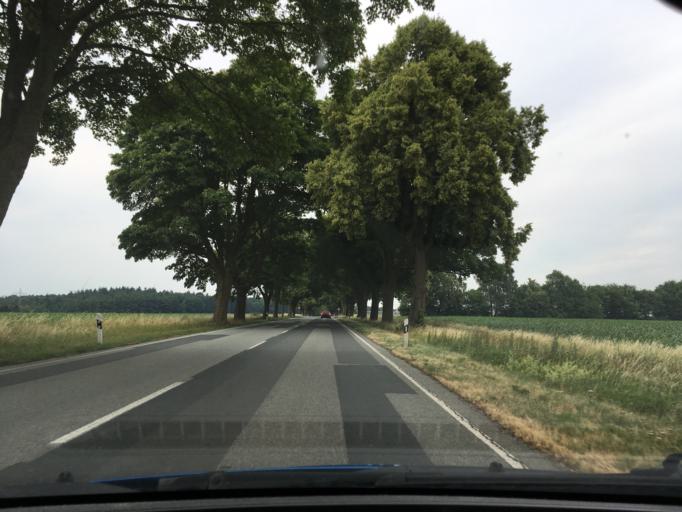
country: DE
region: Lower Saxony
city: Kakenstorf
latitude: 53.3171
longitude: 9.8071
